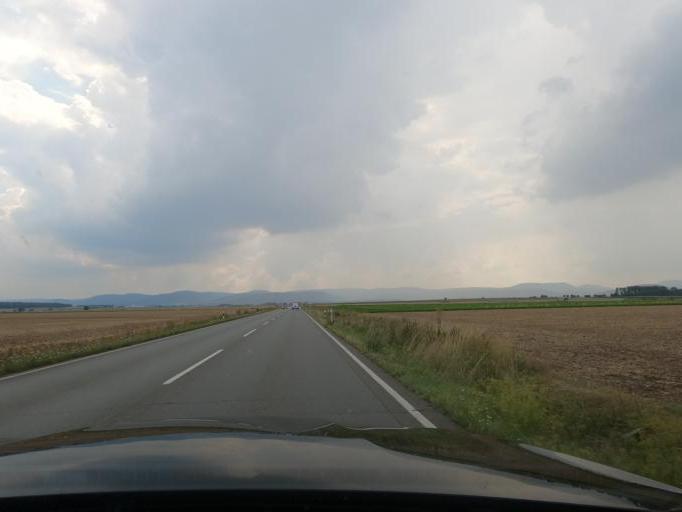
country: DE
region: Lower Saxony
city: Langelsheim
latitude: 51.9745
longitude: 10.3773
